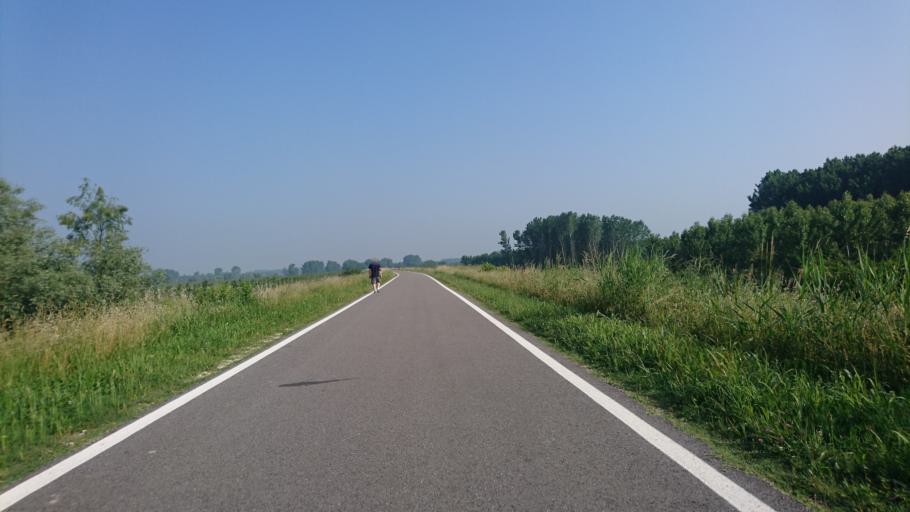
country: IT
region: Veneto
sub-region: Provincia di Rovigo
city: Castelnovo Bariano
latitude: 45.0281
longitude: 11.2713
